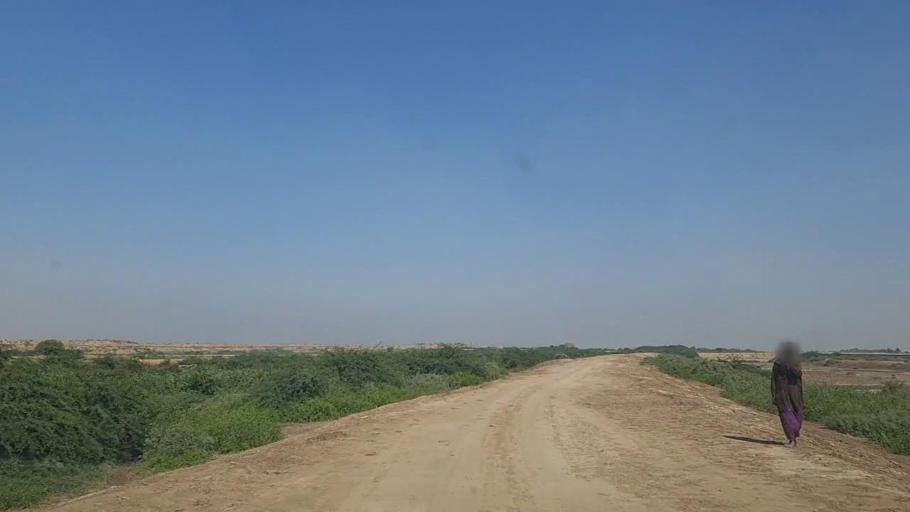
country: PK
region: Sindh
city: Thatta
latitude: 24.8448
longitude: 68.0235
